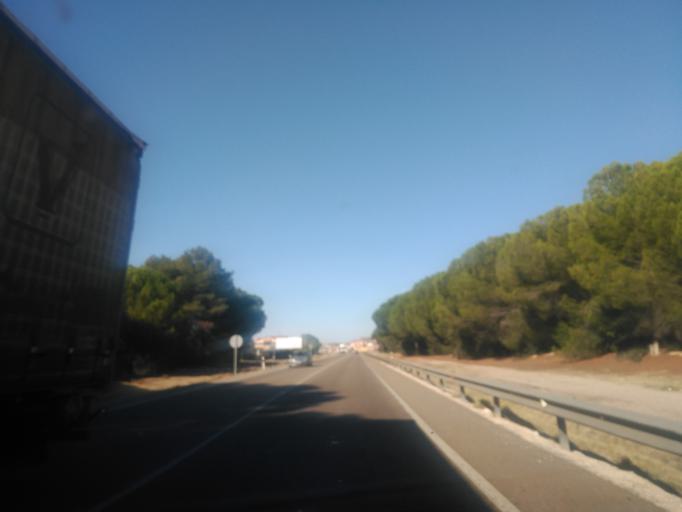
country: ES
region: Castille and Leon
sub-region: Provincia de Valladolid
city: Sardon de Duero
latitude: 41.6069
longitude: -4.4252
